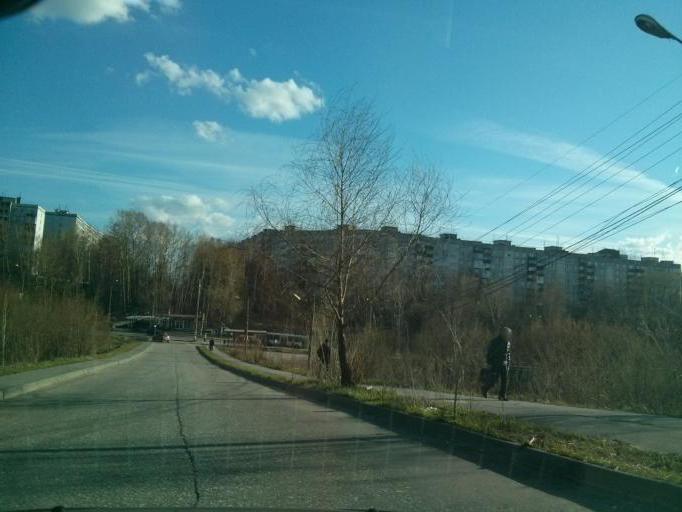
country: RU
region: Nizjnij Novgorod
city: Afonino
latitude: 56.3010
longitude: 44.0679
